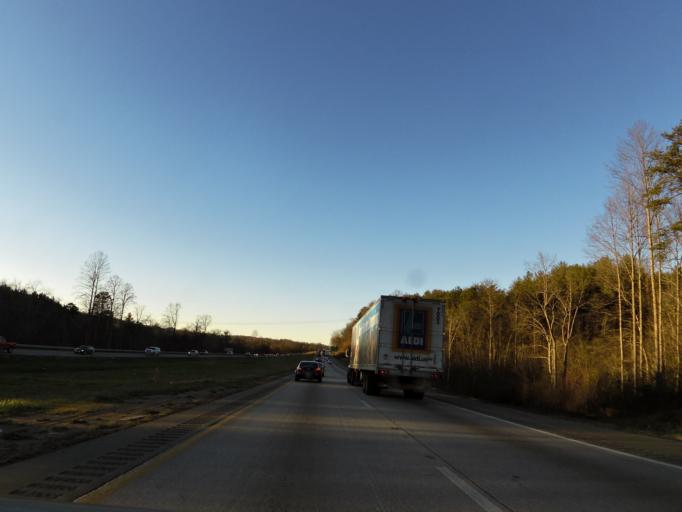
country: US
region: North Carolina
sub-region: Buncombe County
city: Royal Pines
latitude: 35.4623
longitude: -82.5455
